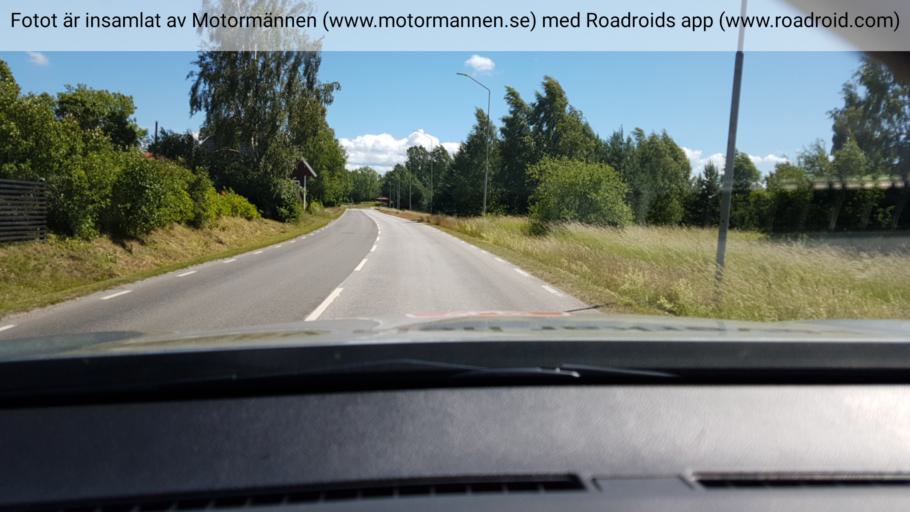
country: SE
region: Vaestra Goetaland
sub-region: Gullspangs Kommun
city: Gullspang
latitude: 58.8333
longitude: 13.9815
